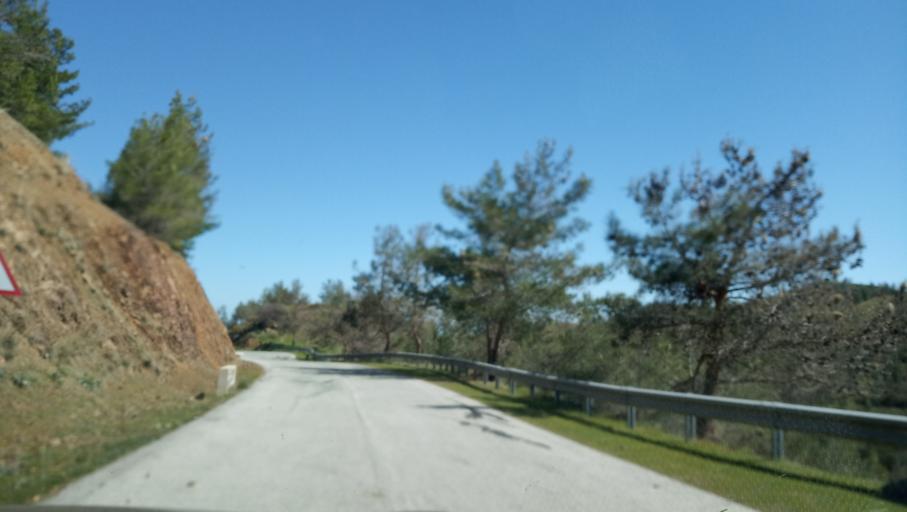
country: CY
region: Lefkosia
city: Lefka
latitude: 35.0839
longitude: 32.7807
